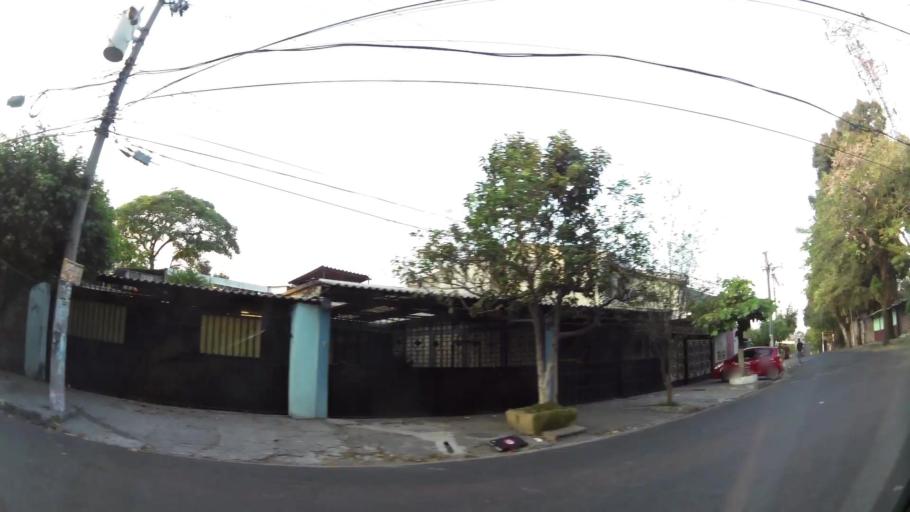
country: SV
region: San Salvador
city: Delgado
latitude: 13.7170
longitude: -89.1846
